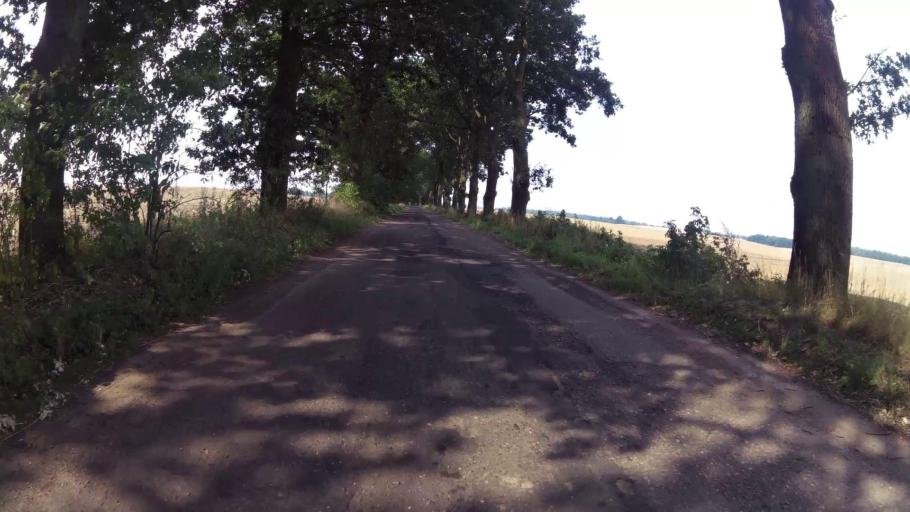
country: PL
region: West Pomeranian Voivodeship
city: Trzcinsko Zdroj
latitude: 52.9344
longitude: 14.6821
